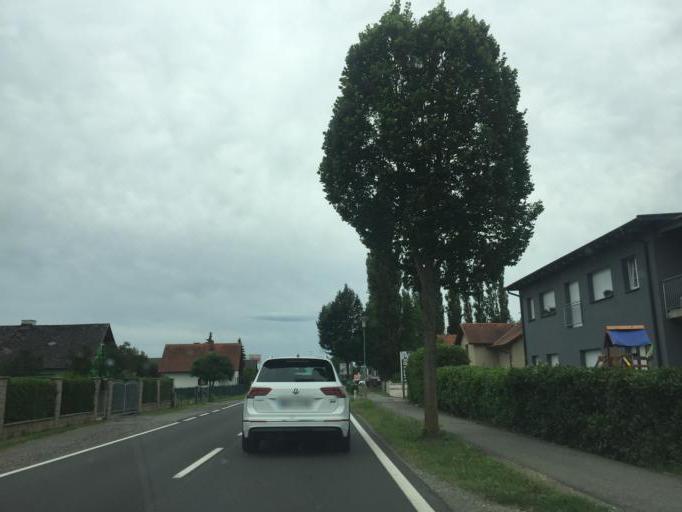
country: AT
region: Styria
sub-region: Politischer Bezirk Leibnitz
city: Kaindorf an der Sulm
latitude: 46.8053
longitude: 15.5531
